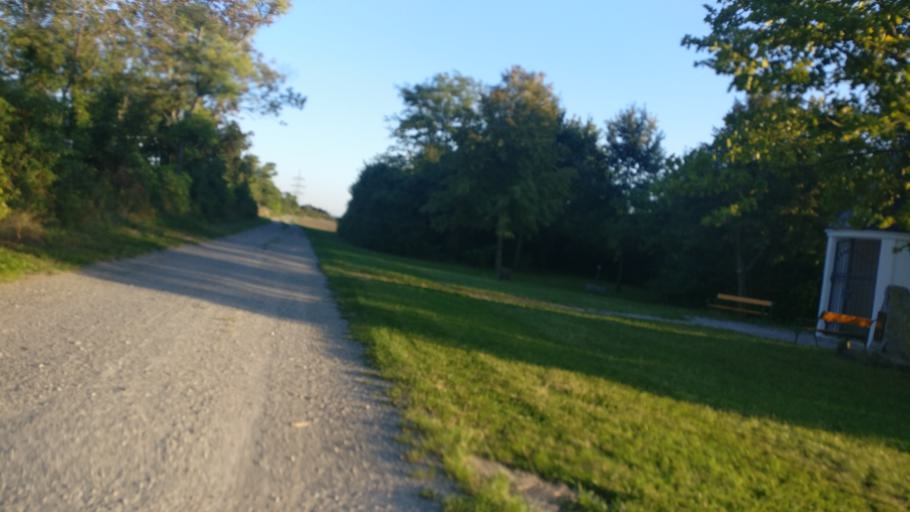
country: AT
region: Lower Austria
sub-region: Politischer Bezirk Modling
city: Munchendorf
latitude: 48.0181
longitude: 16.3769
